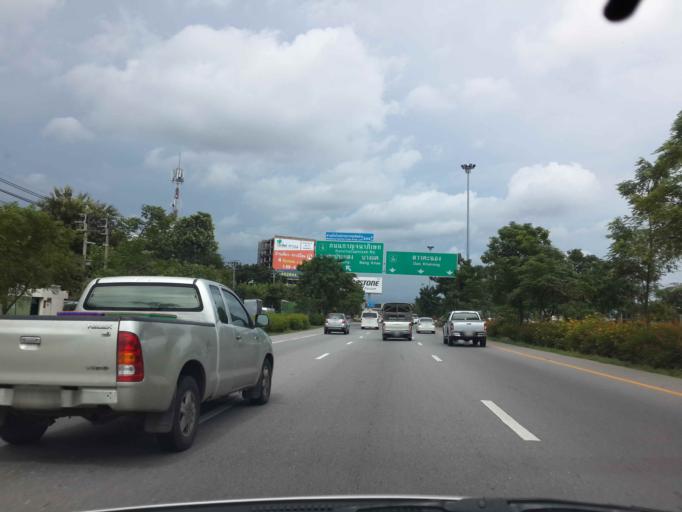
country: TH
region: Bangkok
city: Bang Bon
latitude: 13.6365
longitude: 100.4036
